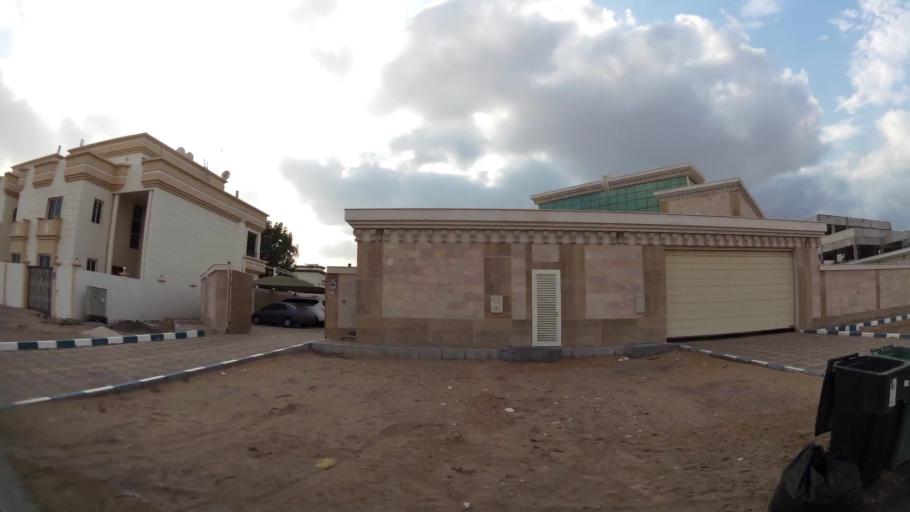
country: AE
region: Abu Dhabi
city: Abu Dhabi
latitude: 24.3683
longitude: 54.5440
